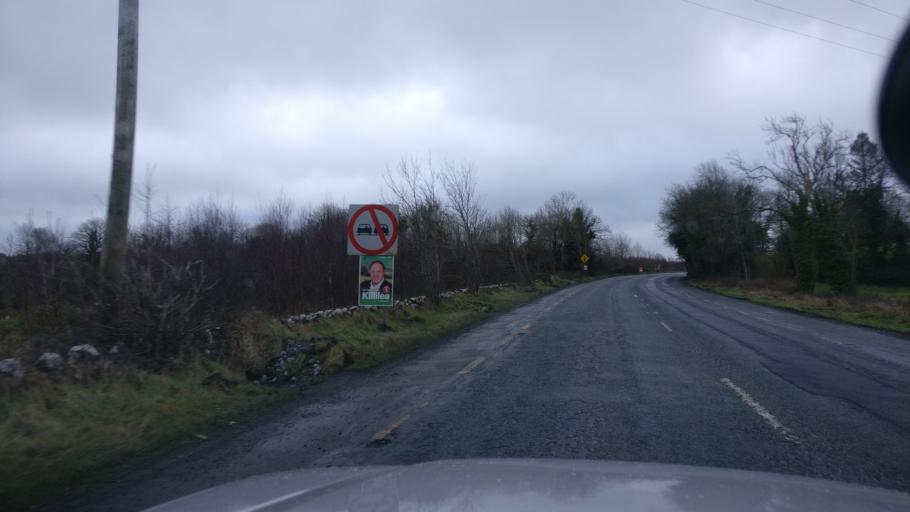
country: IE
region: Connaught
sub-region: County Galway
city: Athenry
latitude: 53.2233
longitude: -8.7211
